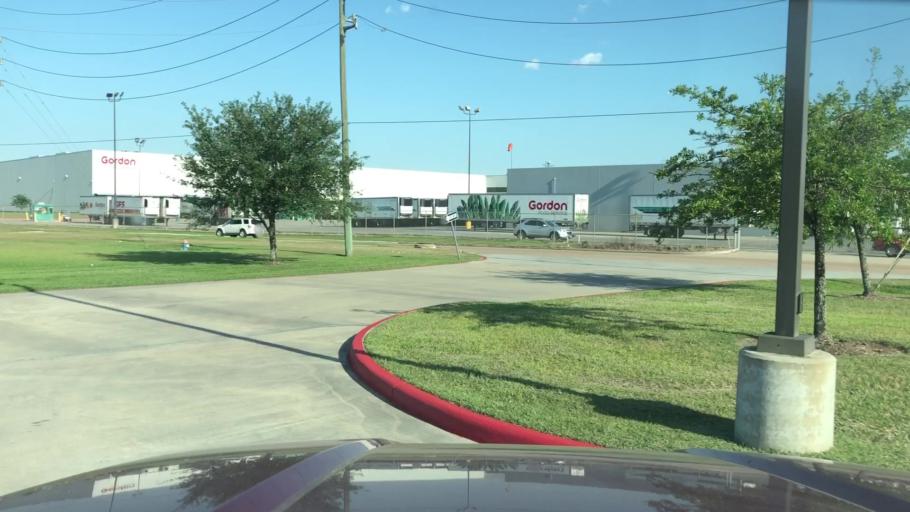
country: US
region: Texas
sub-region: Harris County
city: Hudson
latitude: 29.9427
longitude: -95.4868
